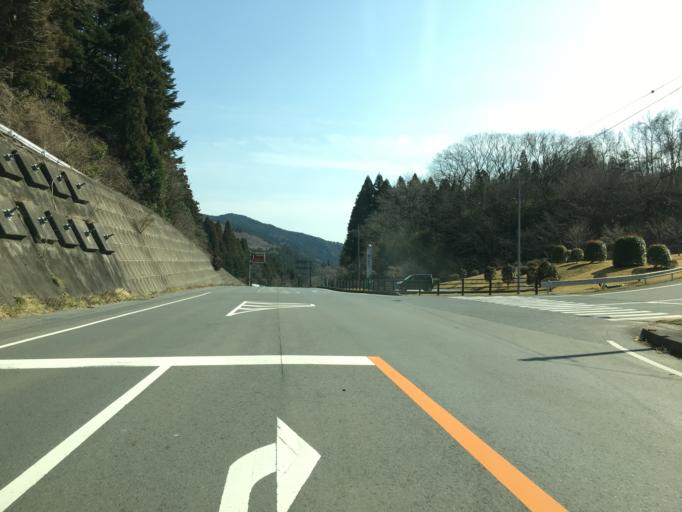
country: JP
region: Ibaraki
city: Daigo
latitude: 36.7955
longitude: 140.4749
